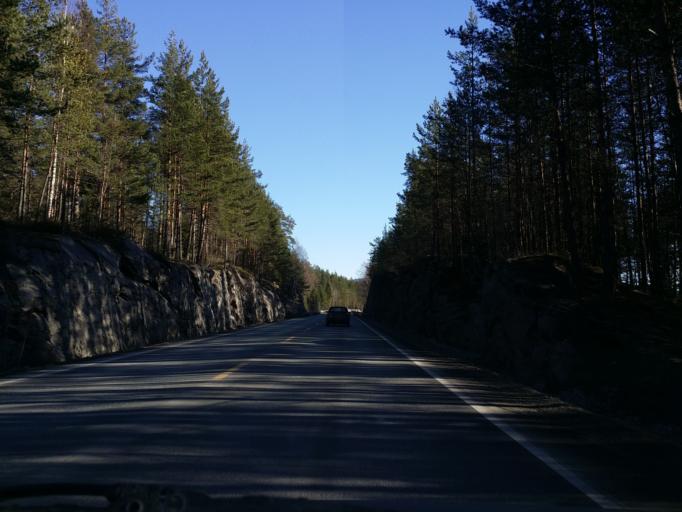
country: NO
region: Buskerud
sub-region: Ringerike
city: Honefoss
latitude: 60.2266
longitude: 10.2473
